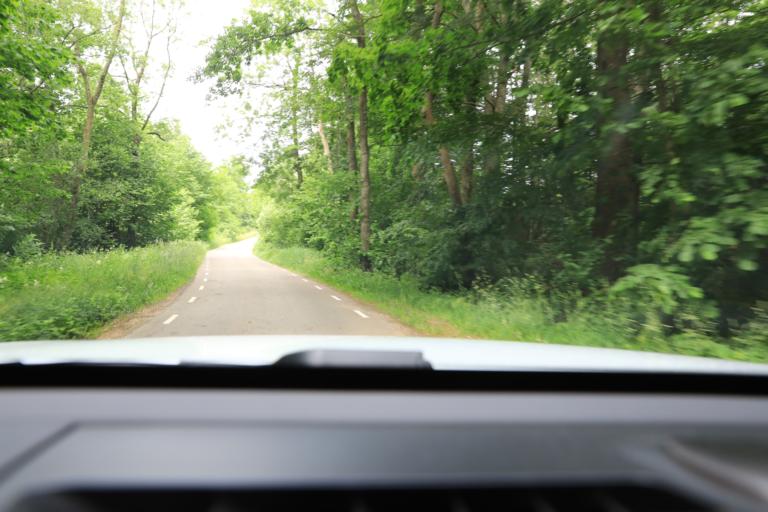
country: SE
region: Halland
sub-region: Varbergs Kommun
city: Tvaaker
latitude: 57.0437
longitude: 12.4669
